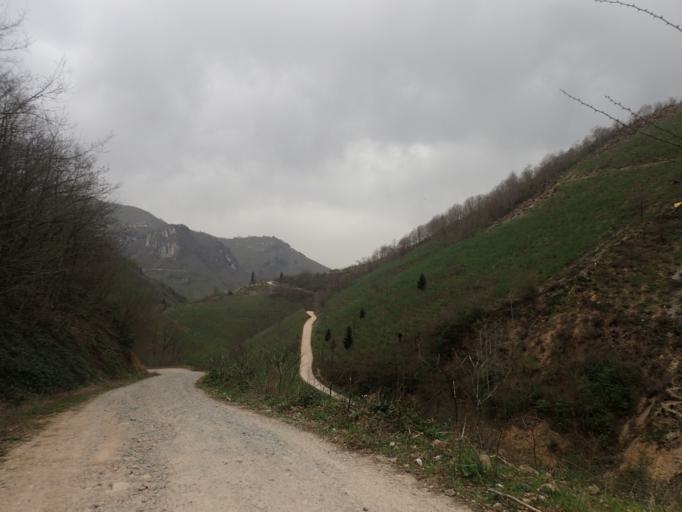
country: TR
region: Ordu
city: Kabaduz
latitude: 40.7876
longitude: 37.8948
